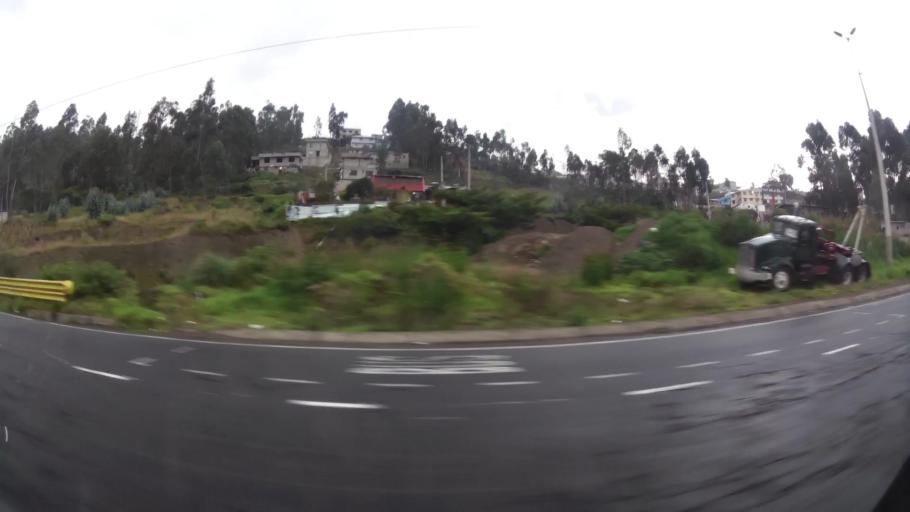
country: EC
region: Pichincha
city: Quito
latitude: -0.1306
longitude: -78.4482
